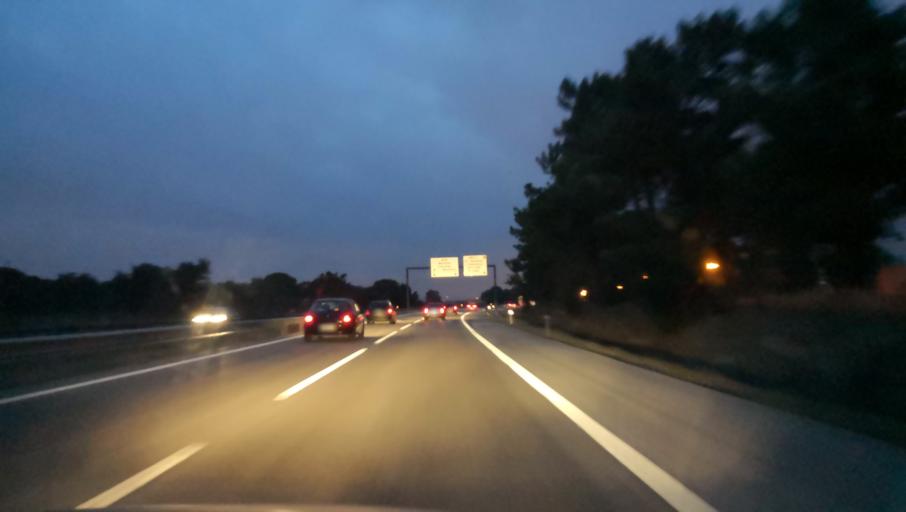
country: PT
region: Setubal
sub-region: Barreiro
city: Santo Antonio da Charneca
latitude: 38.6191
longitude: -9.0324
